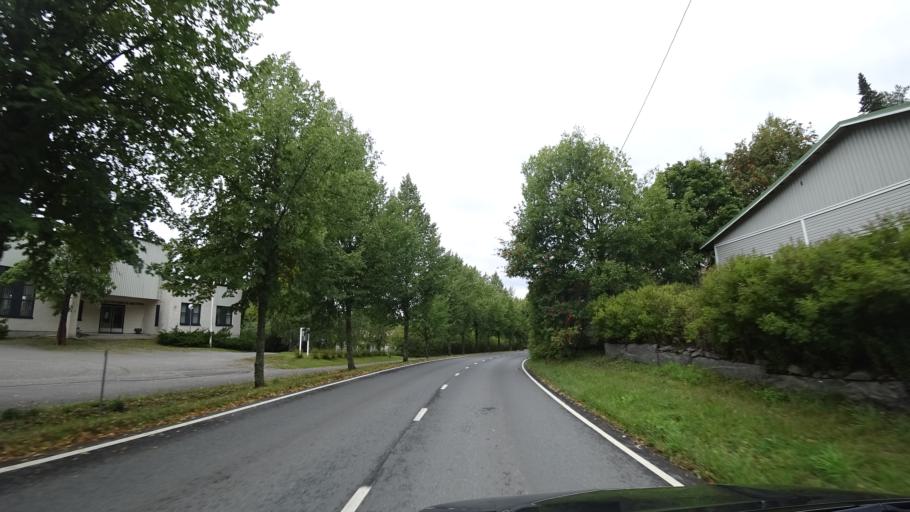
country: FI
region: Haeme
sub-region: Haemeenlinna
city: Lammi
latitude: 61.0837
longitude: 25.0075
